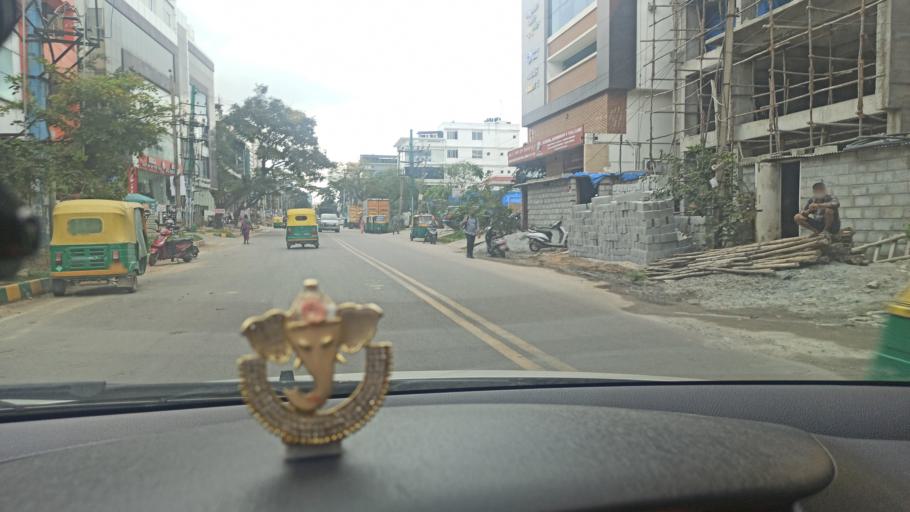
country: IN
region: Karnataka
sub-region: Bangalore Urban
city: Bangalore
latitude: 12.9105
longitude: 77.6324
